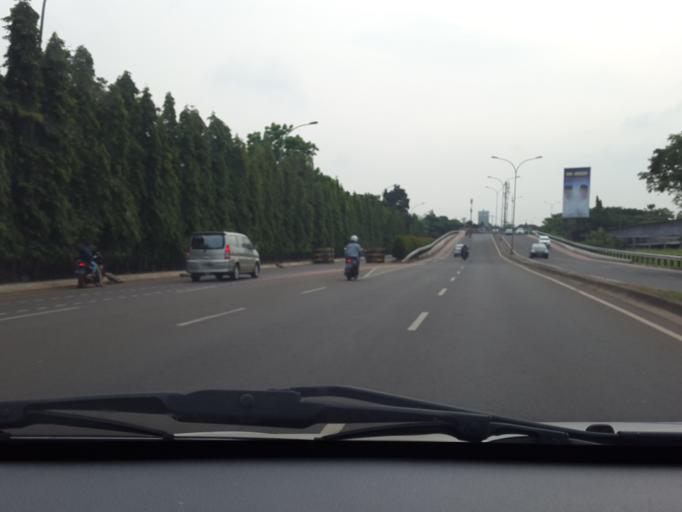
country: ID
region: Banten
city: South Tangerang
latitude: -6.2747
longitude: 106.7087
